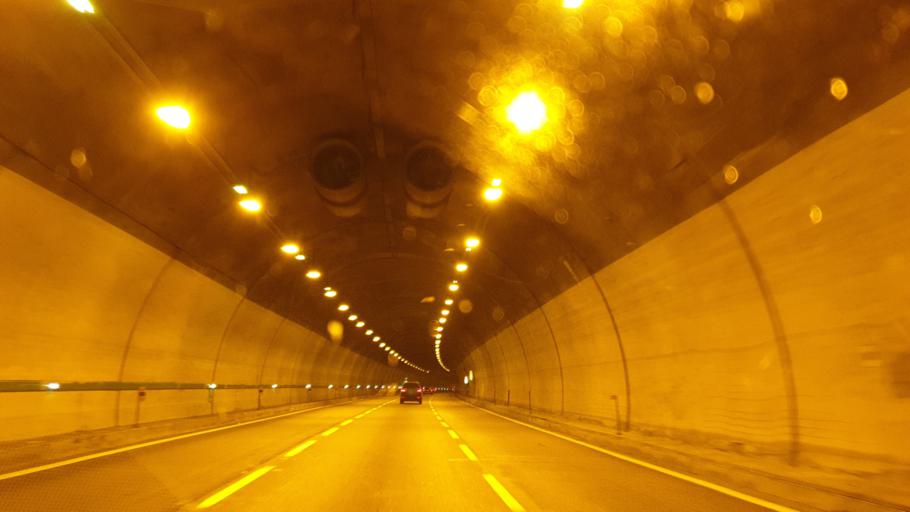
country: IT
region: Emilia-Romagna
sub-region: Provincia di Bologna
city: Sasso Marconi
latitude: 44.3711
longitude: 11.2578
